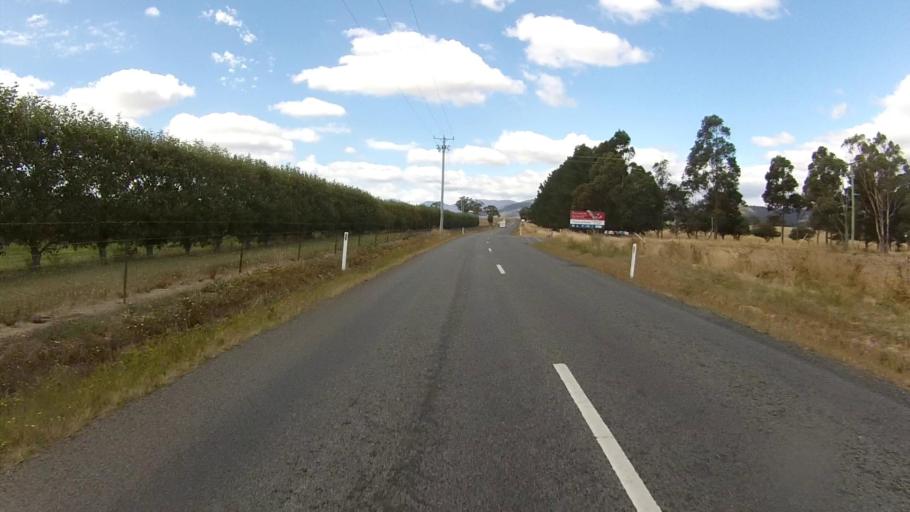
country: AU
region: Tasmania
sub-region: Derwent Valley
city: New Norfolk
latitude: -42.7492
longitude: 146.9739
